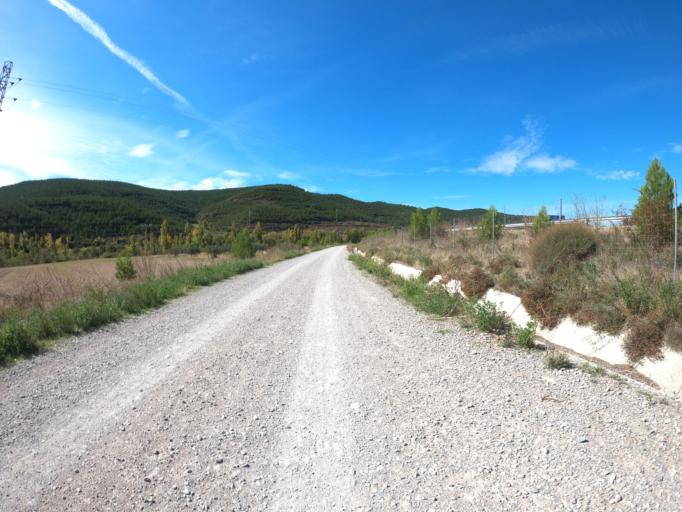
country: ES
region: Navarre
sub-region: Provincia de Navarra
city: Liedena
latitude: 42.6178
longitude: -1.2839
